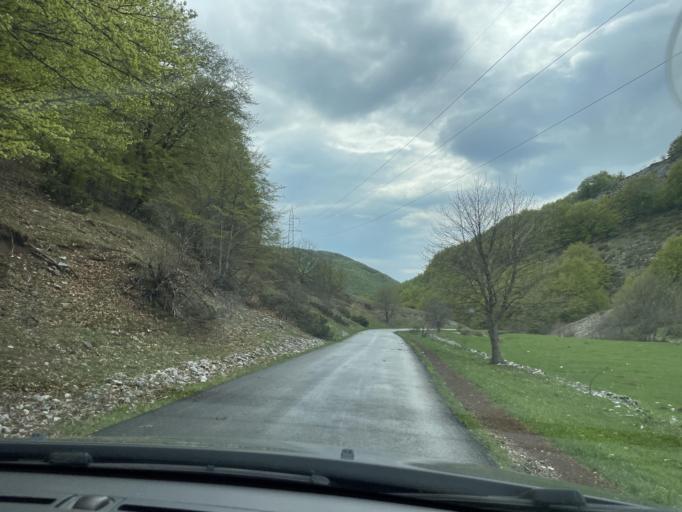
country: MK
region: Opstina Rostusa
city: Rostusha
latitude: 41.6000
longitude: 20.6770
